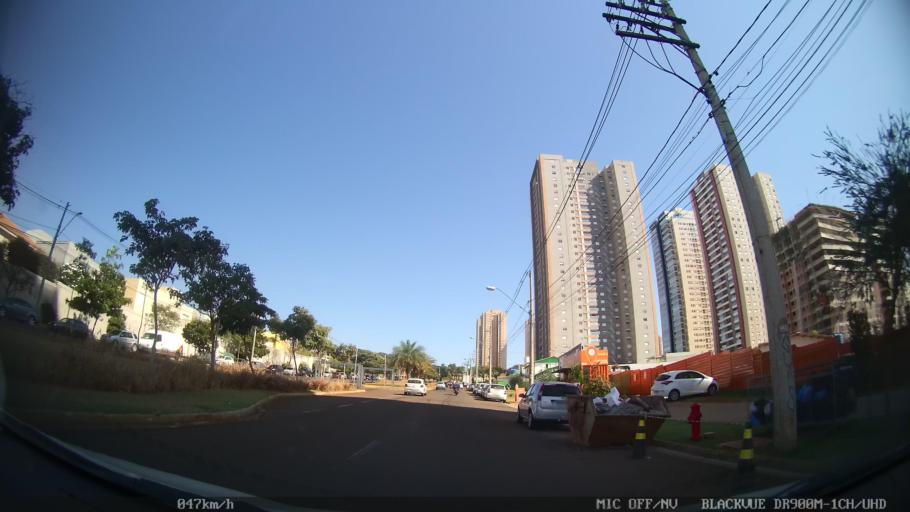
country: BR
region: Sao Paulo
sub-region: Ribeirao Preto
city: Ribeirao Preto
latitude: -21.2192
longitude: -47.7986
